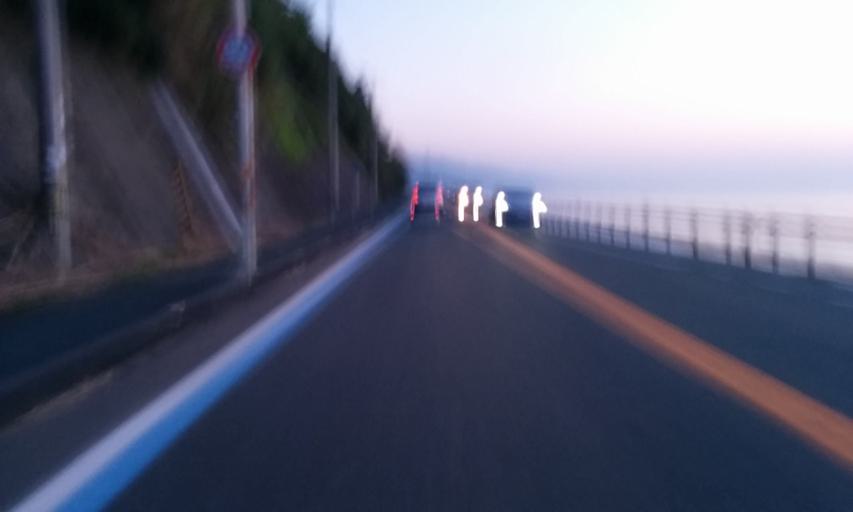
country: JP
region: Ehime
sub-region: Nishiuwa-gun
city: Ikata-cho
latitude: 33.5699
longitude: 132.4351
